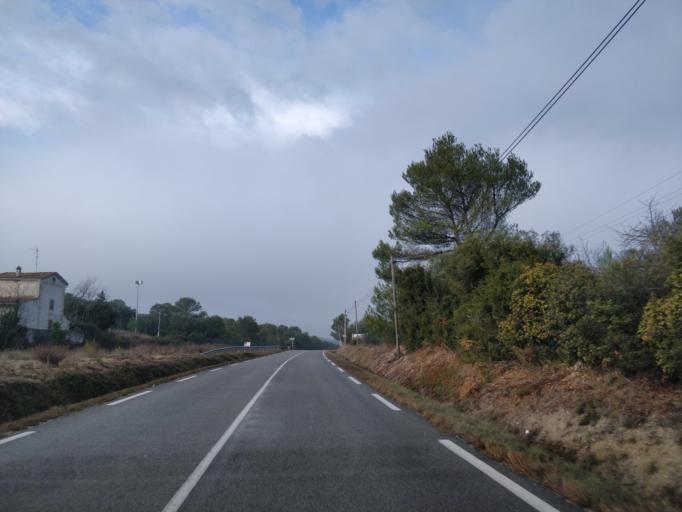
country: FR
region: Languedoc-Roussillon
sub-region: Departement du Gard
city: Caveirac
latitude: 43.8674
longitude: 4.3026
